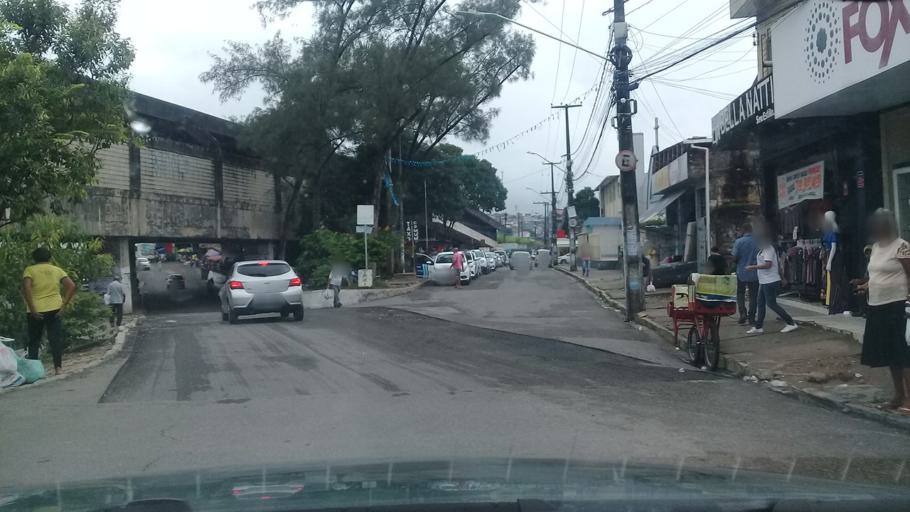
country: BR
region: Pernambuco
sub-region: Jaboatao Dos Guararapes
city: Jaboatao dos Guararapes
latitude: -8.0944
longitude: -34.9728
